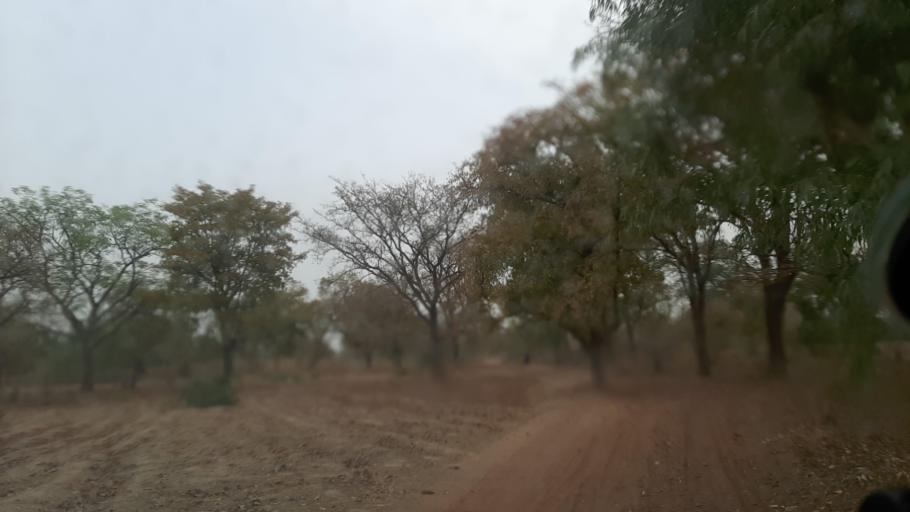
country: BF
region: Boucle du Mouhoun
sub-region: Province des Banwa
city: Salanso
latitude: 11.8504
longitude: -4.4255
